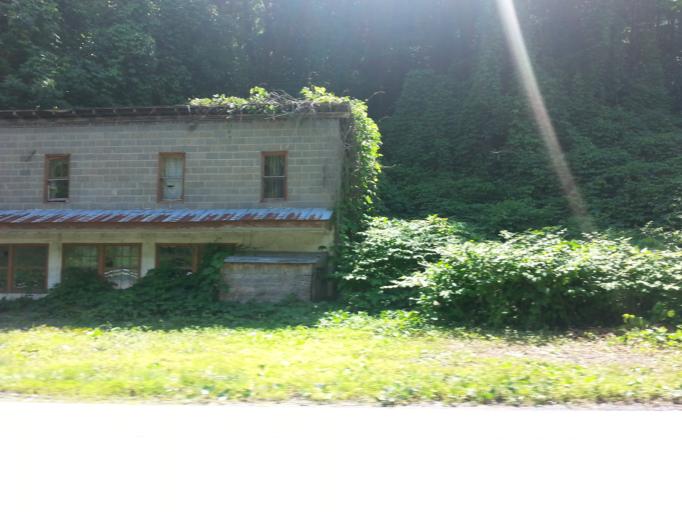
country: US
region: Virginia
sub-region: Lee County
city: Pennington Gap
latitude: 36.7782
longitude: -83.0363
